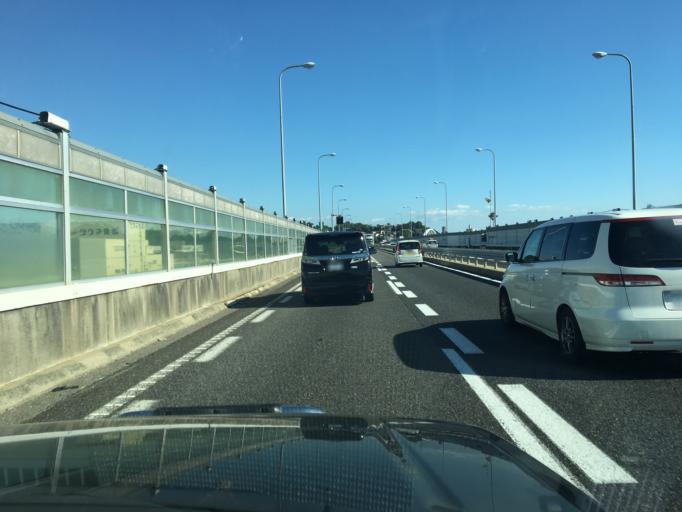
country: JP
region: Aichi
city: Kasugai
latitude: 35.2236
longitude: 136.9693
